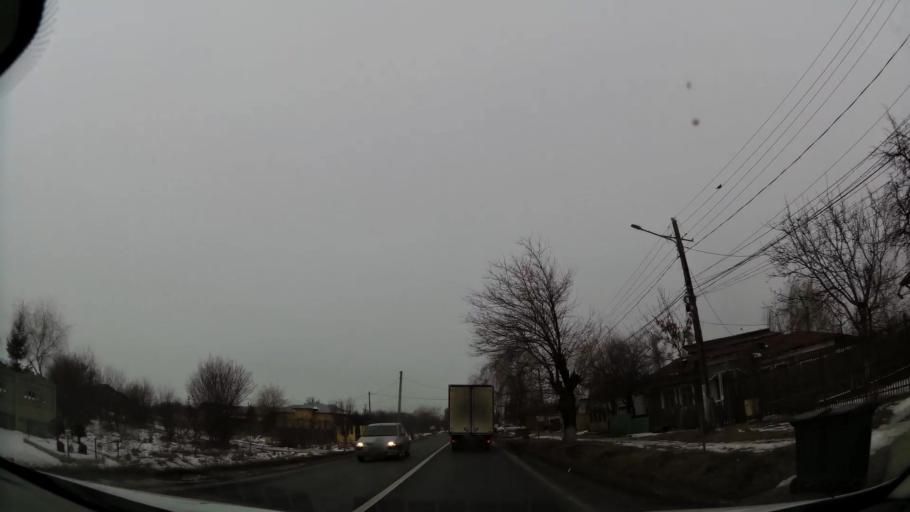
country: RO
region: Dambovita
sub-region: Comuna Tartasesti
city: Baldana
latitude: 44.6024
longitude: 25.7782
